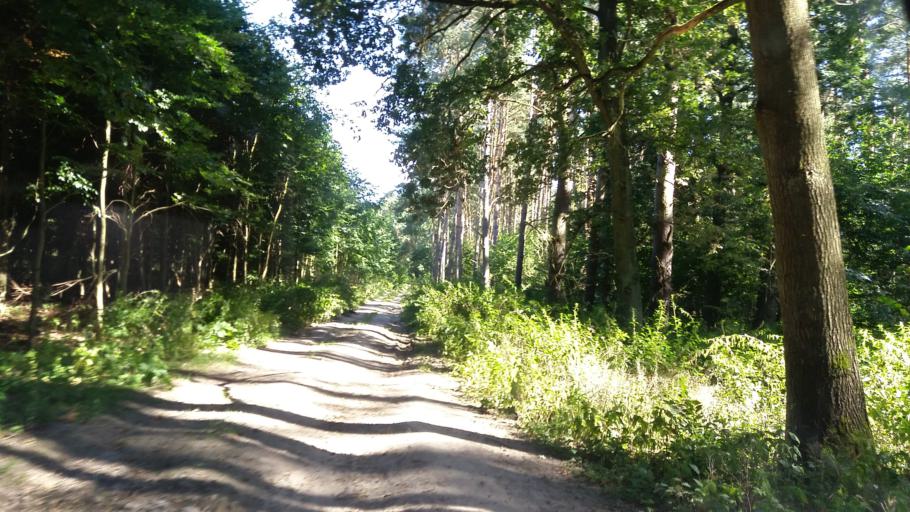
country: PL
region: West Pomeranian Voivodeship
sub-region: Powiat choszczenski
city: Krzecin
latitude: 53.0897
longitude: 15.4399
